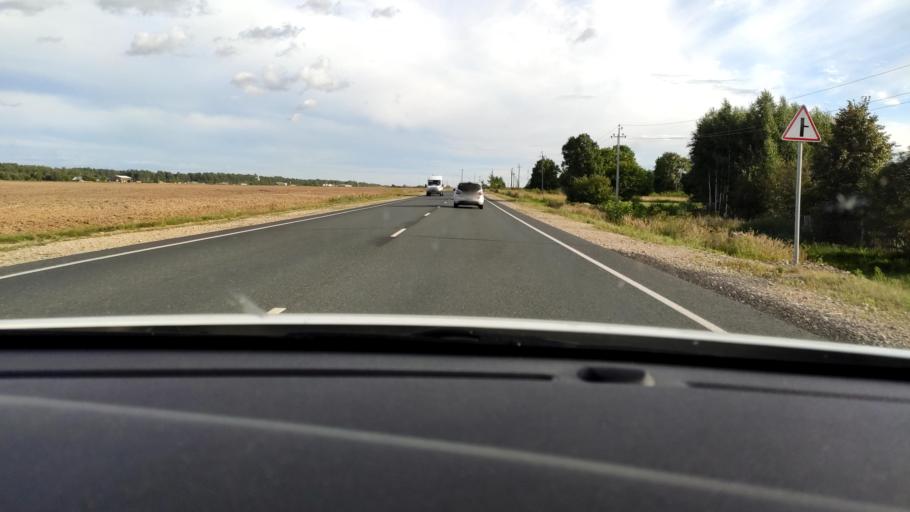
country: RU
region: Mariy-El
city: Suslonger
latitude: 56.2219
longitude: 48.2353
